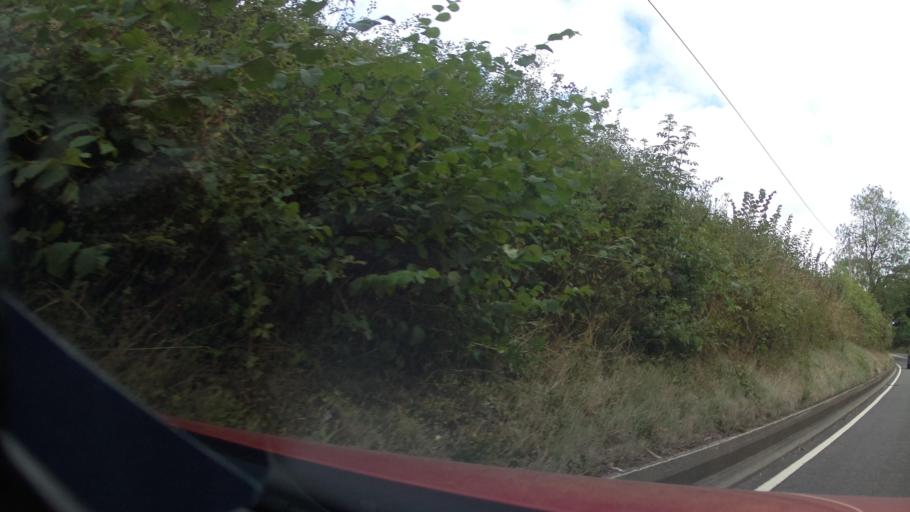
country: GB
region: England
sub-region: Leicestershire
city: Coalville
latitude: 52.7596
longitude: -1.3704
